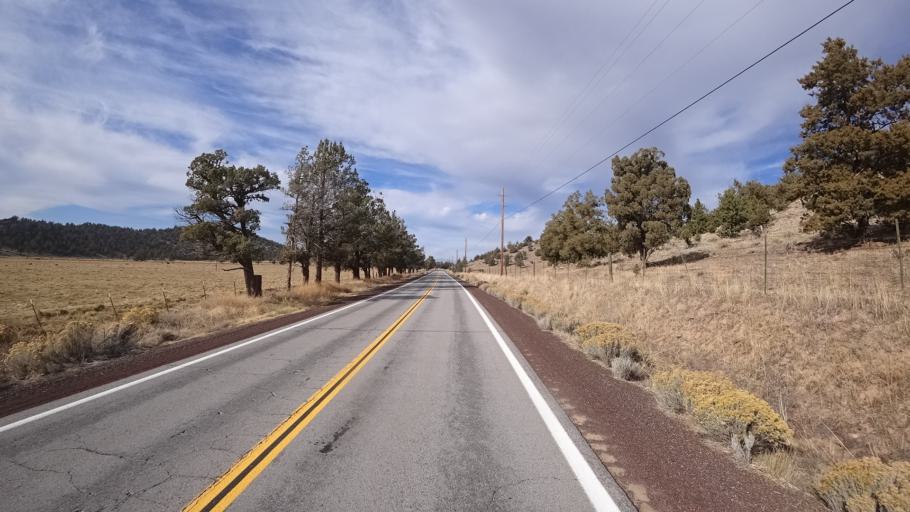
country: US
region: California
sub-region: Siskiyou County
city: Weed
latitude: 41.5717
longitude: -122.3908
